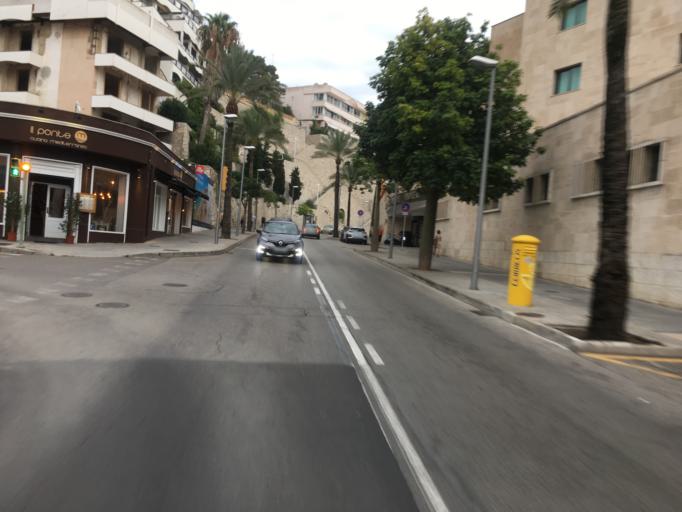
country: ES
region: Balearic Islands
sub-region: Illes Balears
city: Palma
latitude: 39.5528
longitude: 2.6072
